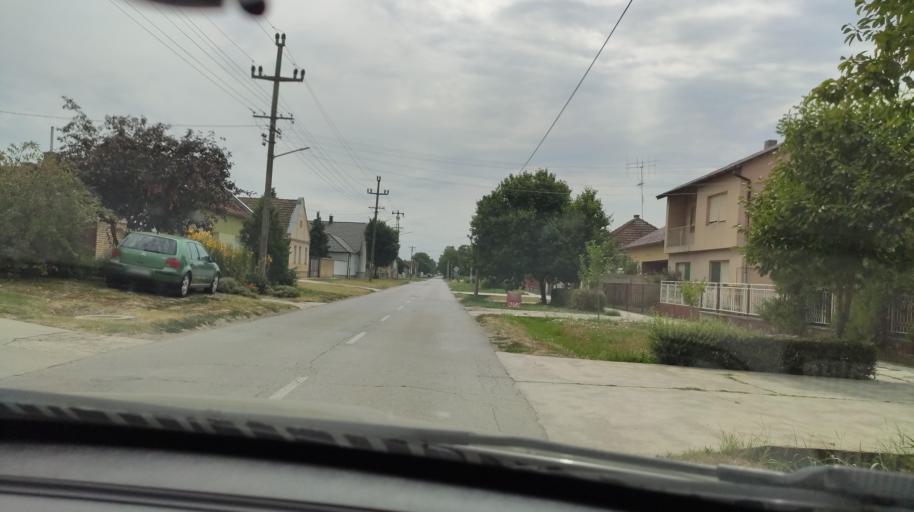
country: RS
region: Autonomna Pokrajina Vojvodina
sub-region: Juznobacki Okrug
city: Temerin
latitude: 45.4154
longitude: 19.8853
